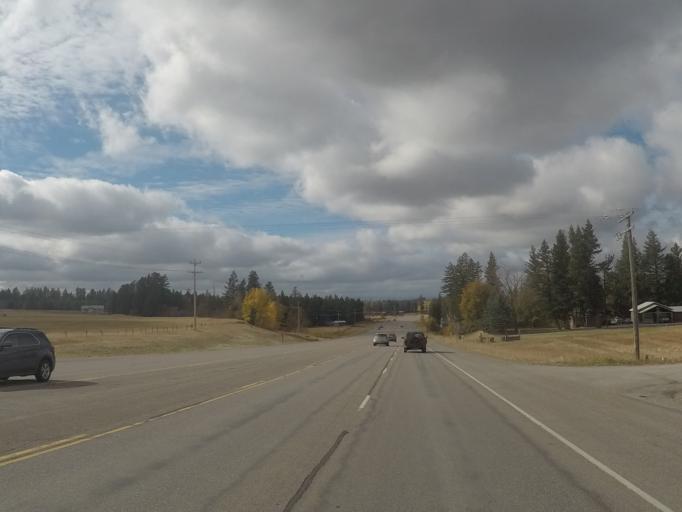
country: US
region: Montana
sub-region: Flathead County
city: Columbia Falls
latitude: 48.3636
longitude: -114.1529
